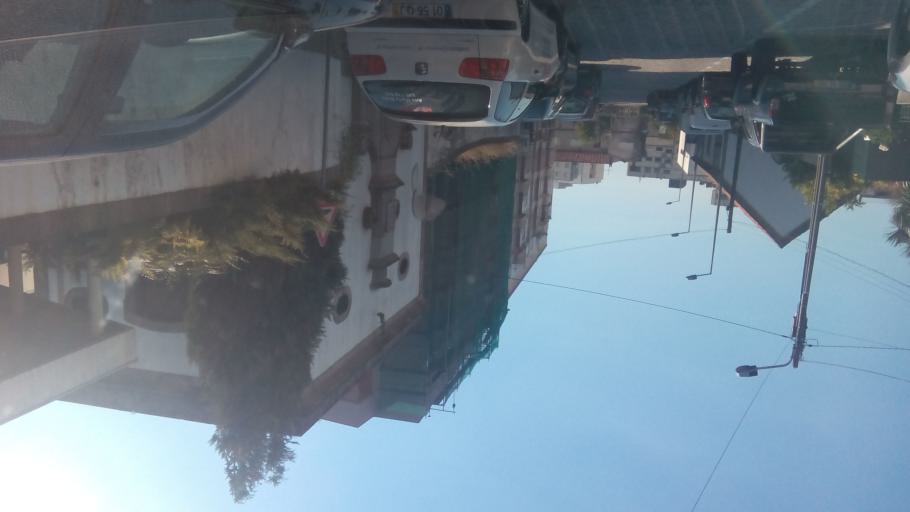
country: PT
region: Porto
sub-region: Paredes
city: Paredes
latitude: 41.2084
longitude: -8.3350
